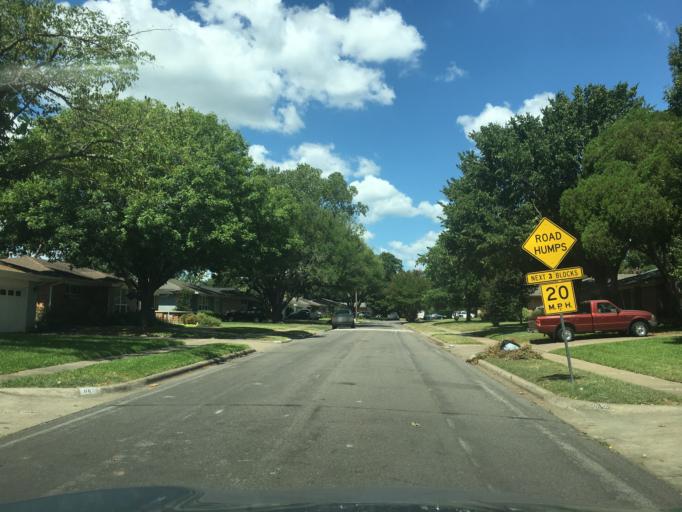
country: US
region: Texas
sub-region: Dallas County
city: Garland
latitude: 32.8683
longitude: -96.7016
